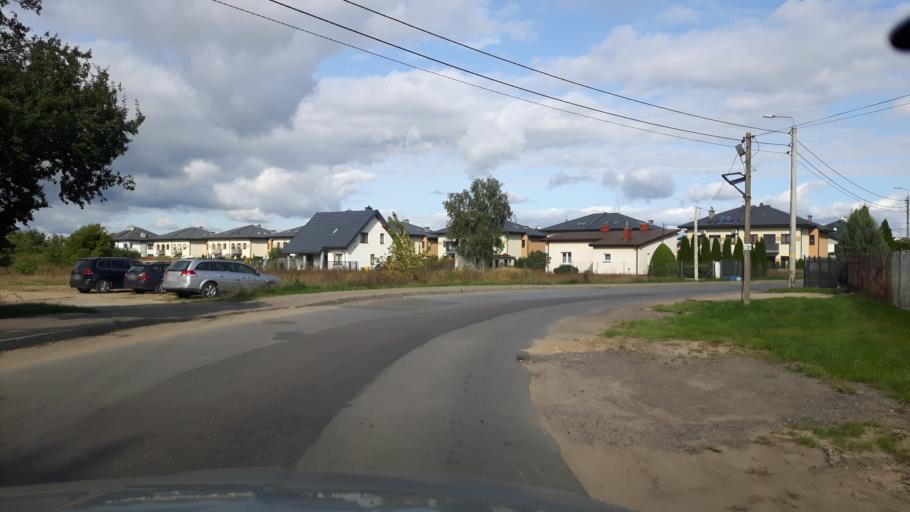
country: PL
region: Masovian Voivodeship
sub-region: Powiat wolominski
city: Marki
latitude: 52.3285
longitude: 21.0935
